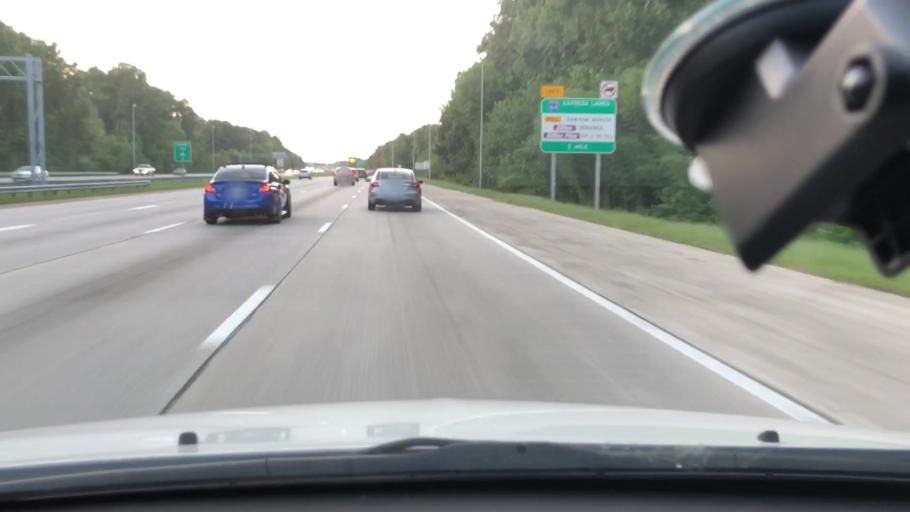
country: US
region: Virginia
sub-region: City of Chesapeake
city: Chesapeake
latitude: 36.8172
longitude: -76.1946
